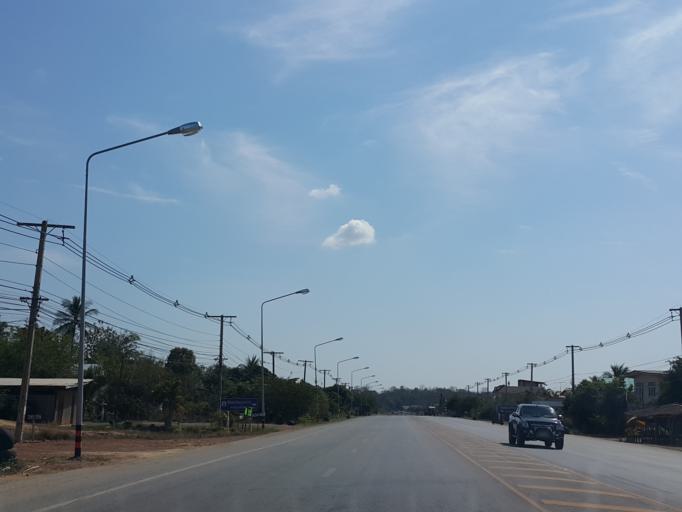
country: TH
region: Sukhothai
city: Thung Saliam
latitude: 17.3241
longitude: 99.6334
